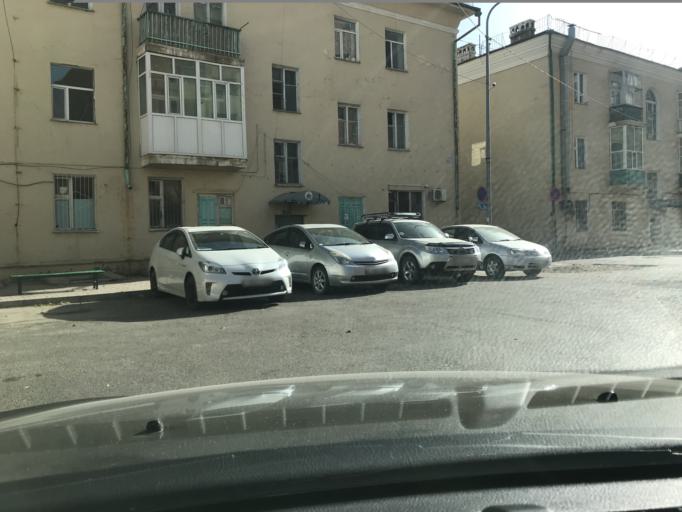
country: MN
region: Ulaanbaatar
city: Ulaanbaatar
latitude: 47.9217
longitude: 106.9103
